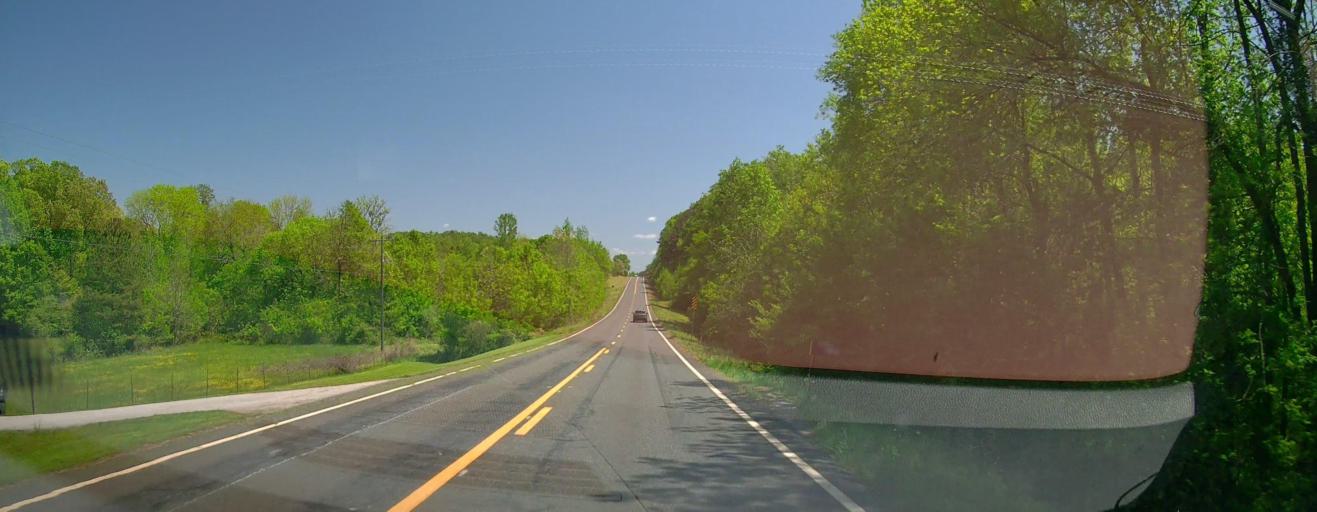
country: US
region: Georgia
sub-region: Jasper County
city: Monticello
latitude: 33.2703
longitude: -83.5886
